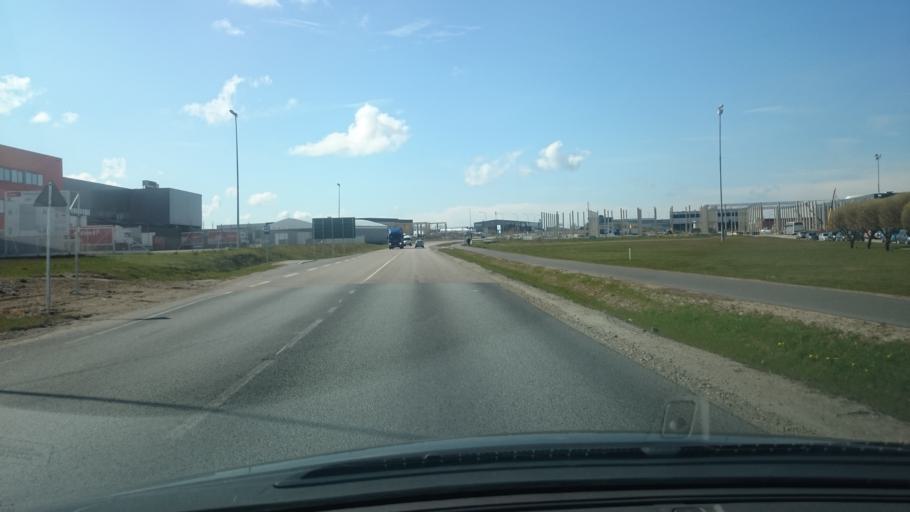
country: EE
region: Harju
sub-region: Rae vald
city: Jueri
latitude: 59.3591
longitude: 24.8879
